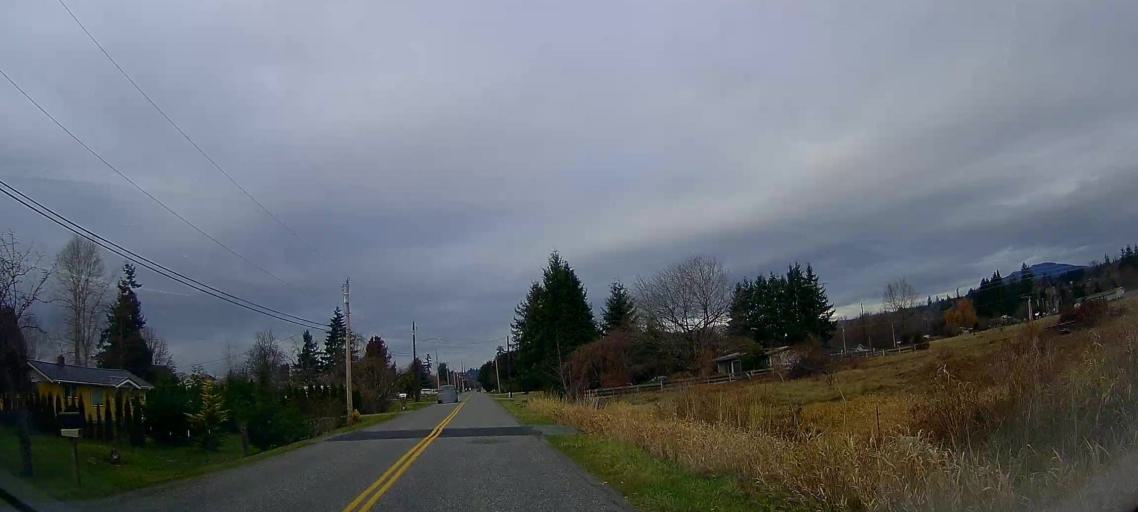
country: US
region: Washington
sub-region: Skagit County
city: Sedro-Woolley
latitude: 48.5123
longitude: -122.2502
